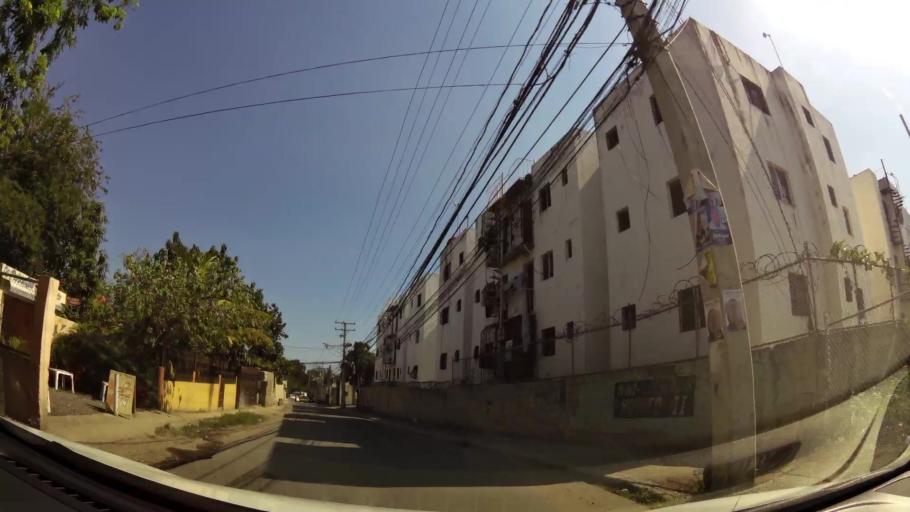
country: DO
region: Santo Domingo
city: Santo Domingo Oeste
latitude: 18.4766
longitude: -70.0010
